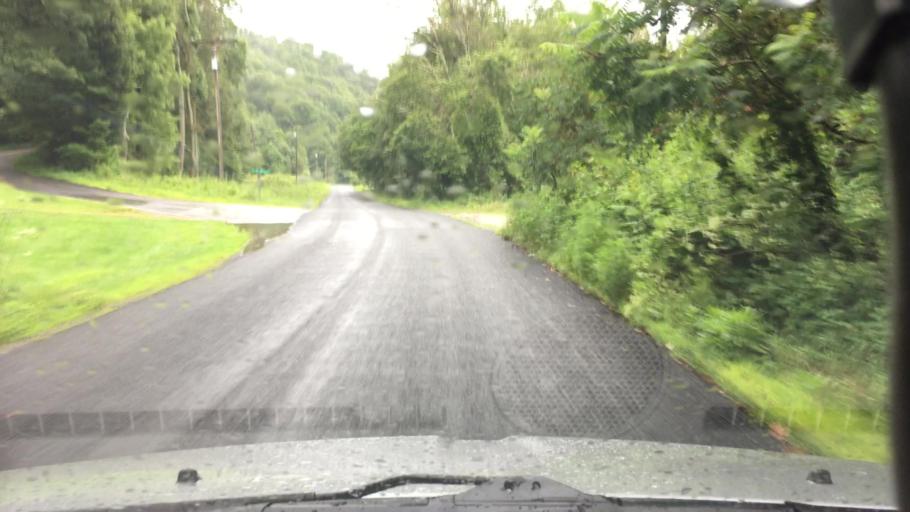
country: US
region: North Carolina
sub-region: Madison County
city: Mars Hill
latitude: 35.9113
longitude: -82.5114
